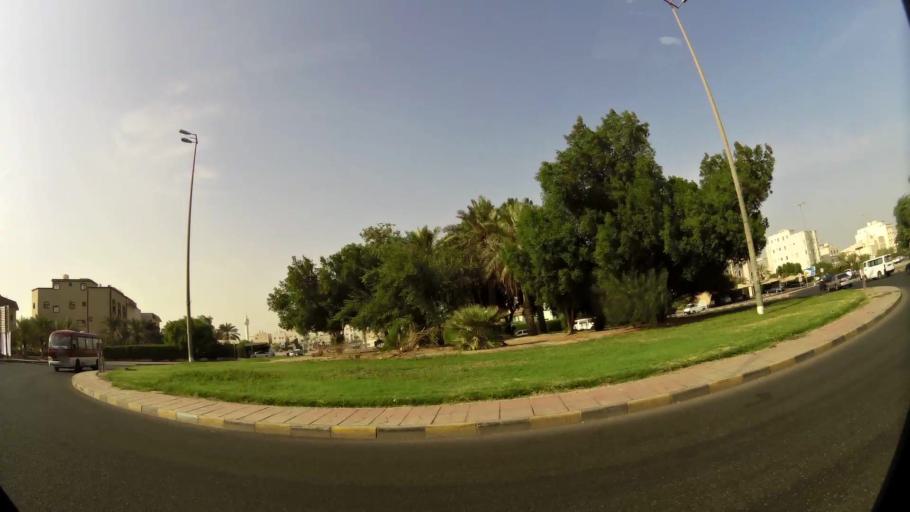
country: KW
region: Mubarak al Kabir
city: Mubarak al Kabir
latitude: 29.1729
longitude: 48.0770
